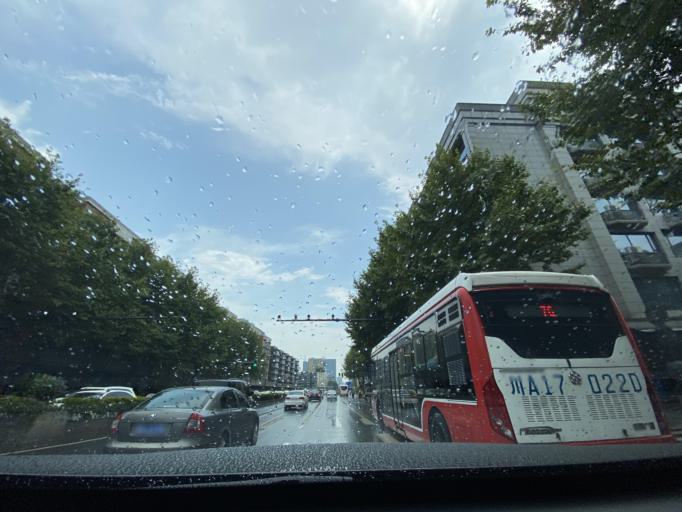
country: CN
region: Sichuan
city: Chengdu
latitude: 30.6421
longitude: 104.0732
